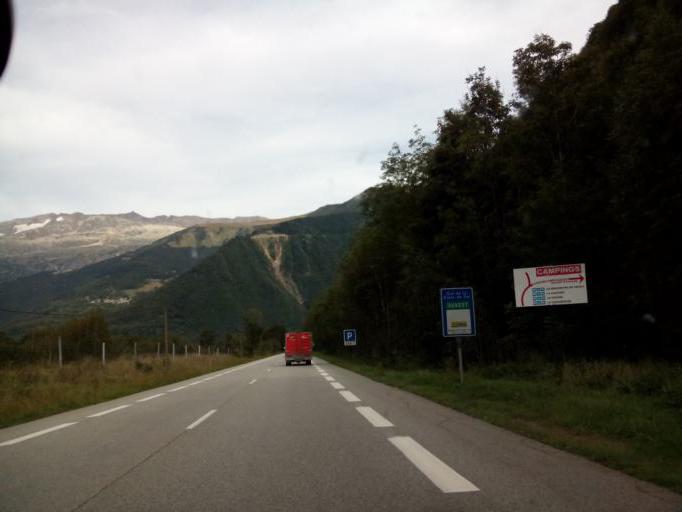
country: FR
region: Rhone-Alpes
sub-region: Departement de l'Isere
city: Livet-et-Gavet
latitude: 45.1153
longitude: 5.9986
